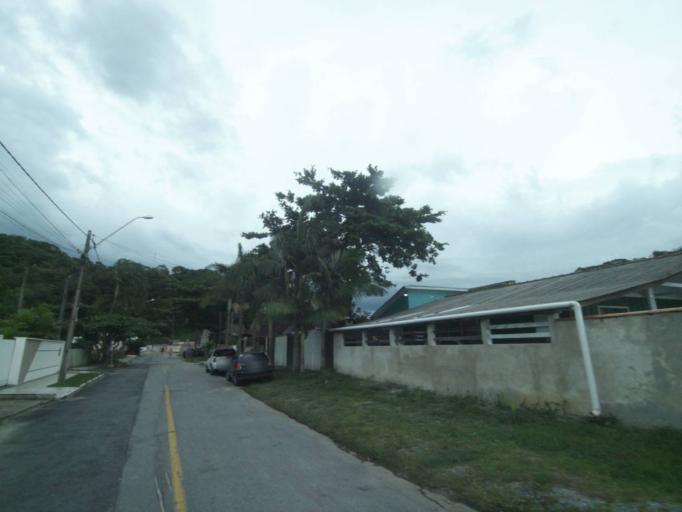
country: BR
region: Parana
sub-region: Guaratuba
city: Guaratuba
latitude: -25.8174
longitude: -48.5409
